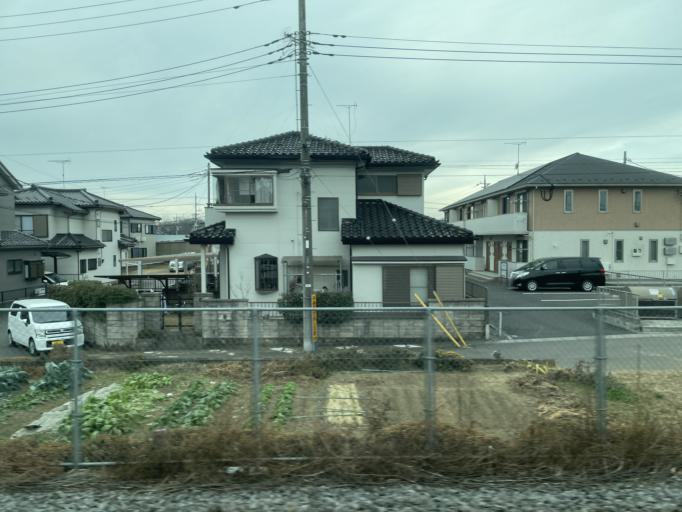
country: JP
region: Ibaraki
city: Koga
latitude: 36.1791
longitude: 139.7141
